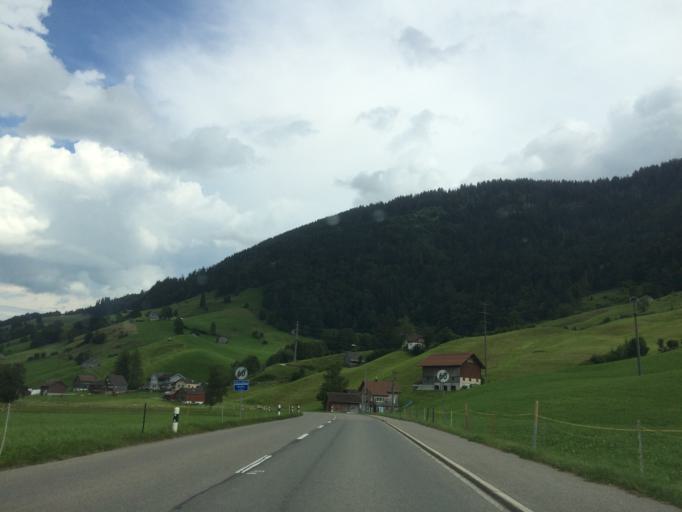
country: CH
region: Saint Gallen
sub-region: Wahlkreis Sarganserland
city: Quarten
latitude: 47.1839
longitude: 9.2572
